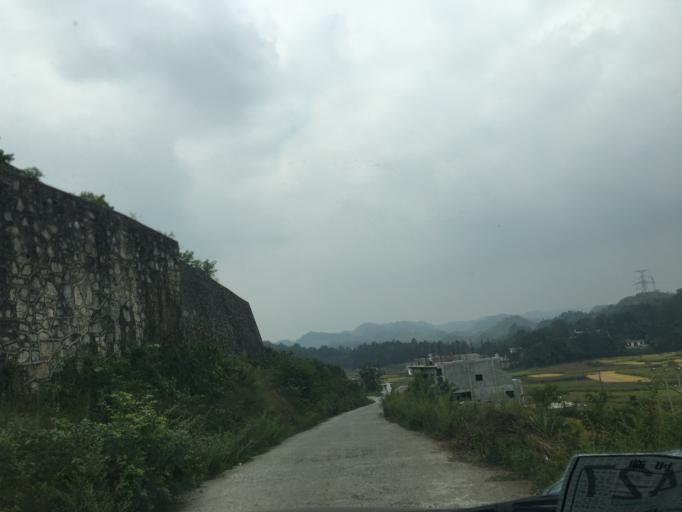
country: CN
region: Guangxi Zhuangzu Zizhiqu
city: Xinzhou
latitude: 25.5677
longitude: 105.6133
